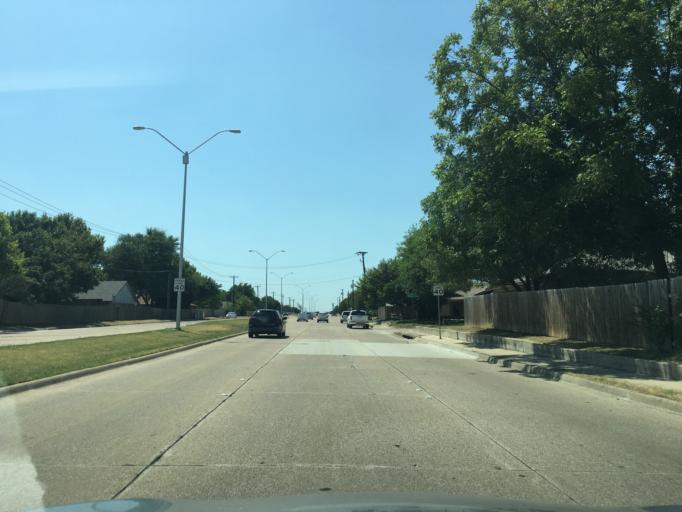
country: US
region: Texas
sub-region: Tarrant County
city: Edgecliff Village
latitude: 32.6350
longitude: -97.3616
